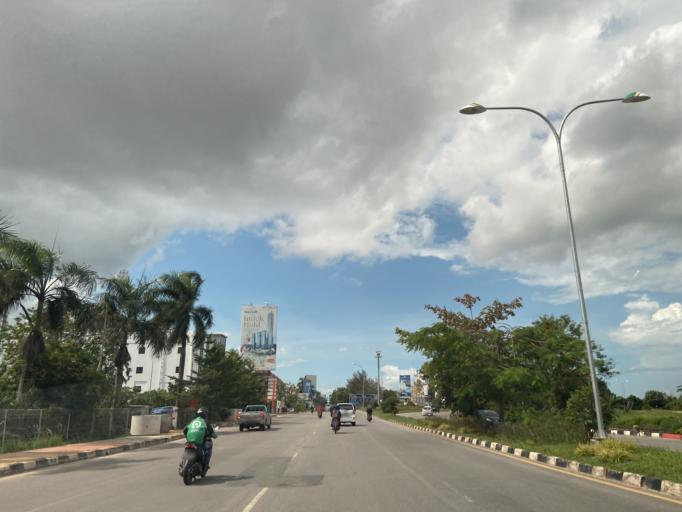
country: SG
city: Singapore
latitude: 1.1333
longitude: 104.0421
